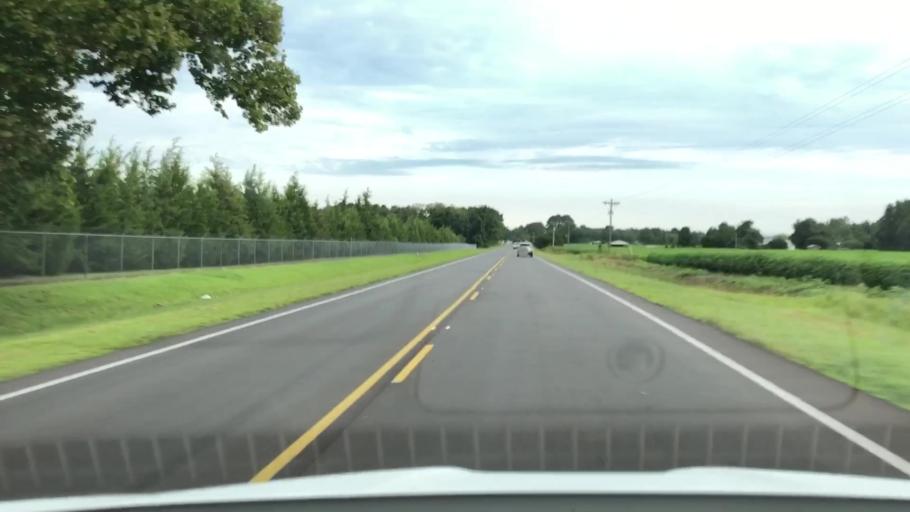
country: US
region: North Carolina
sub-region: Jones County
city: Maysville
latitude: 34.8929
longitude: -77.2164
